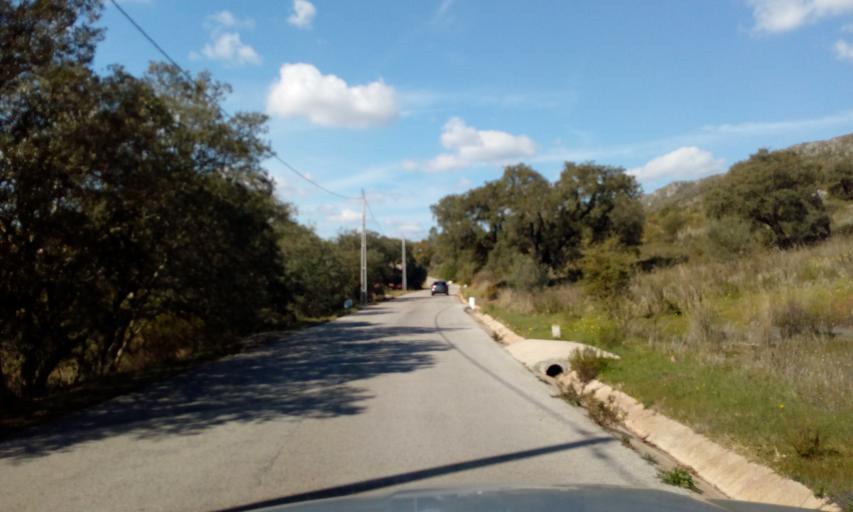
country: PT
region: Faro
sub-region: Loule
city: Loule
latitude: 37.2465
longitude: -8.0816
